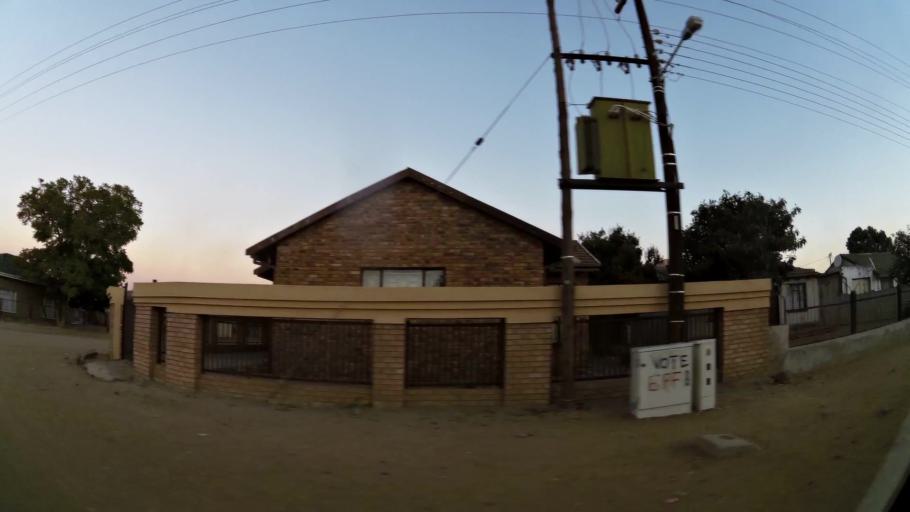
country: ZA
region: Limpopo
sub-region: Capricorn District Municipality
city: Polokwane
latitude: -23.8585
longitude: 29.3912
